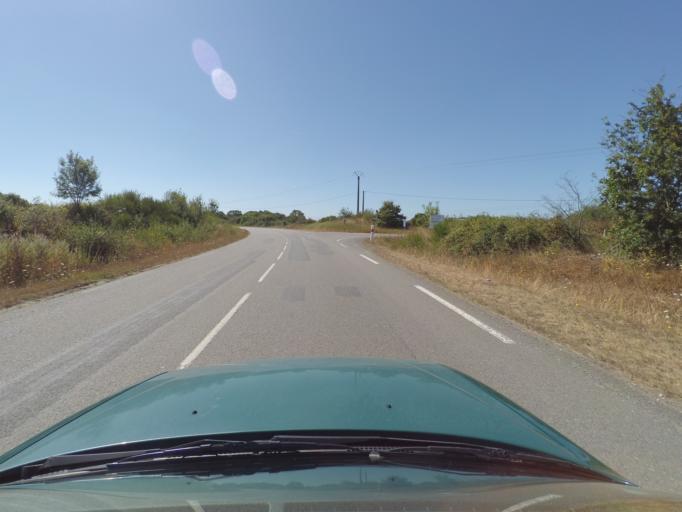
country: FR
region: Pays de la Loire
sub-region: Departement de la Loire-Atlantique
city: Les Sorinieres
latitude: 47.1309
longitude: -1.5159
